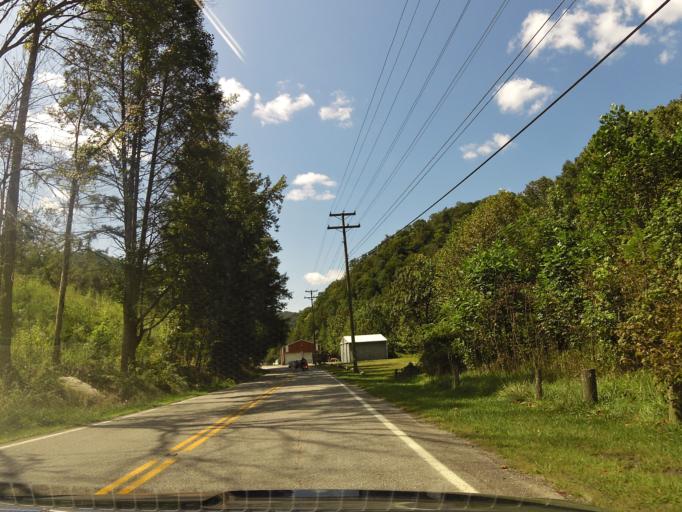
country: US
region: Kentucky
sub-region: Harlan County
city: Loyall
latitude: 36.9819
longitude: -83.4013
